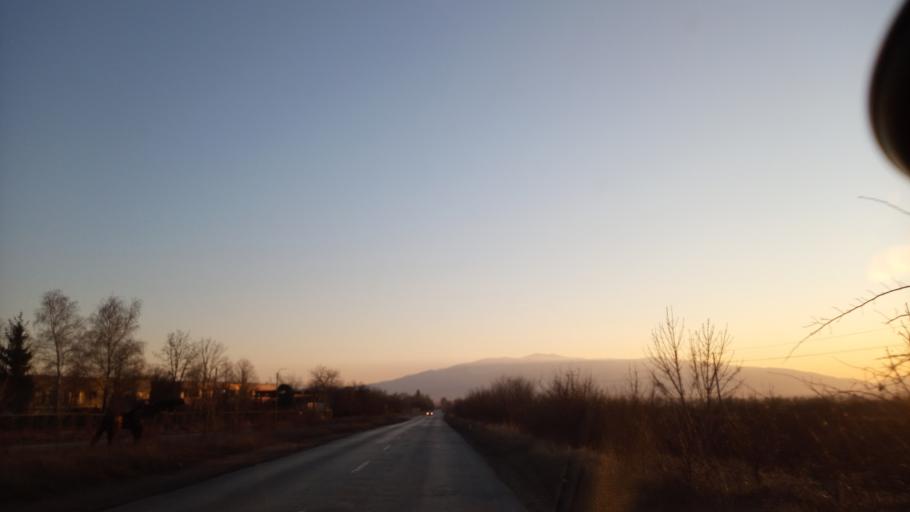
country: BG
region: Sofia-Capital
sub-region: Stolichna Obshtina
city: Bukhovo
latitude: 42.7606
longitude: 23.4876
